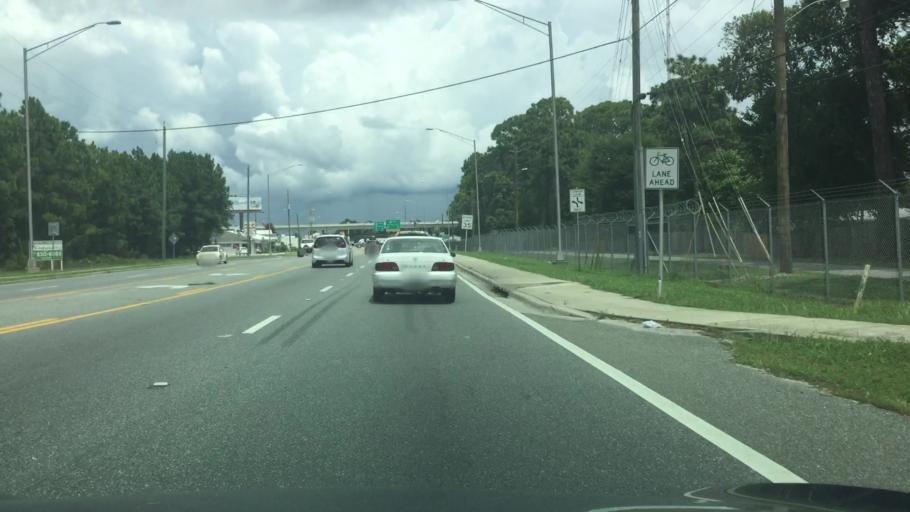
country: US
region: Florida
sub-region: Bay County
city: Upper Grand Lagoon
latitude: 30.1841
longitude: -85.7608
